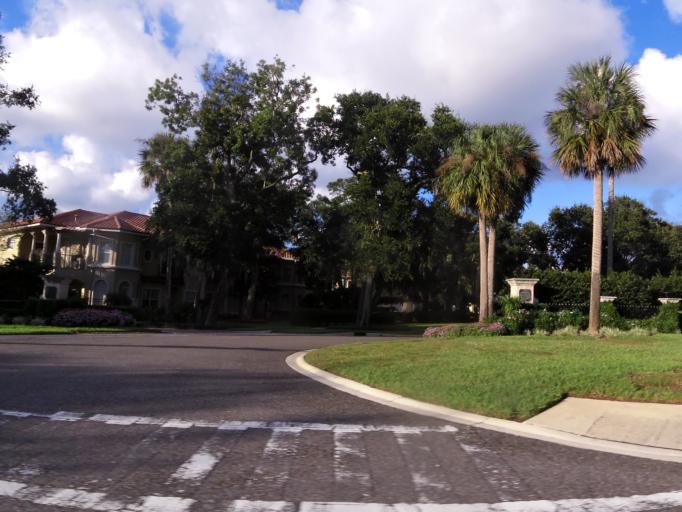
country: US
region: Florida
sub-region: Saint Johns County
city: Palm Valley
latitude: 30.1595
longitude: -81.3652
